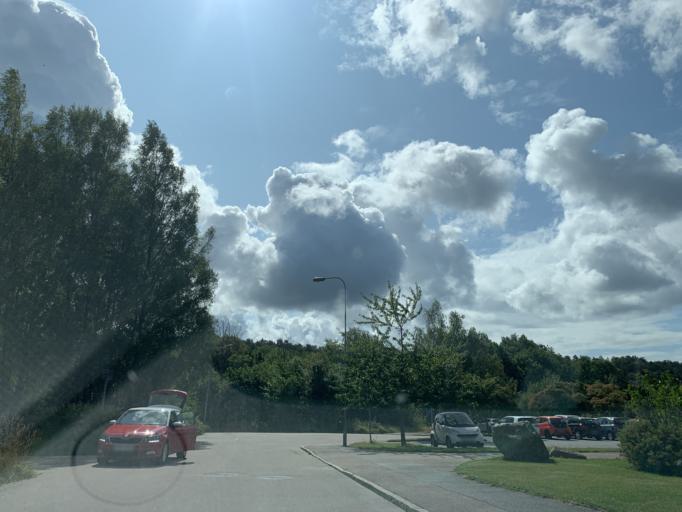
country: SE
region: Vaestra Goetaland
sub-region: Goteborg
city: Eriksbo
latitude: 57.7709
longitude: 12.0460
